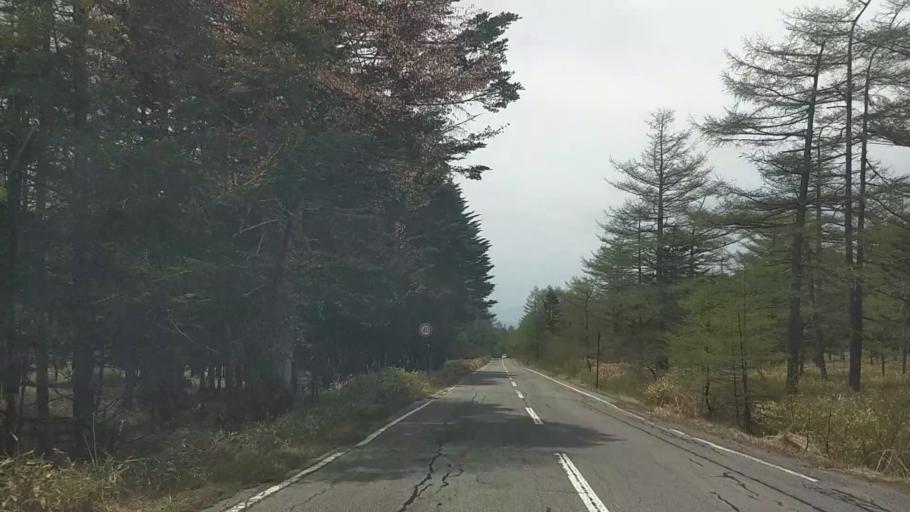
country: JP
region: Nagano
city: Chino
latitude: 36.0531
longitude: 138.3183
